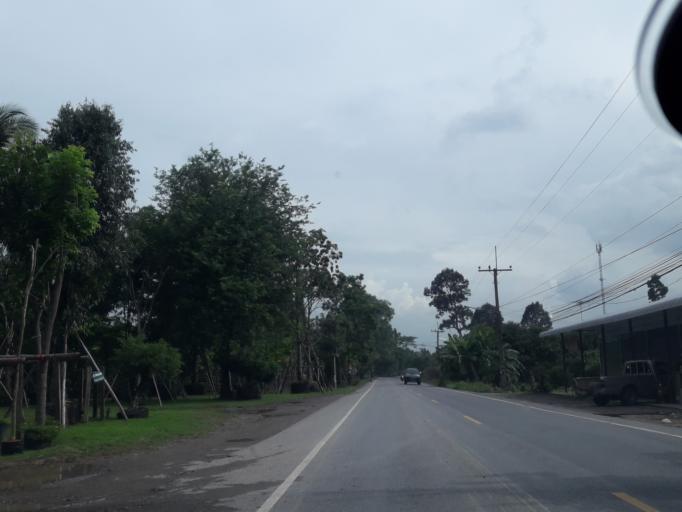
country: TH
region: Sara Buri
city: Wihan Daeng
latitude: 14.4099
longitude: 101.1086
